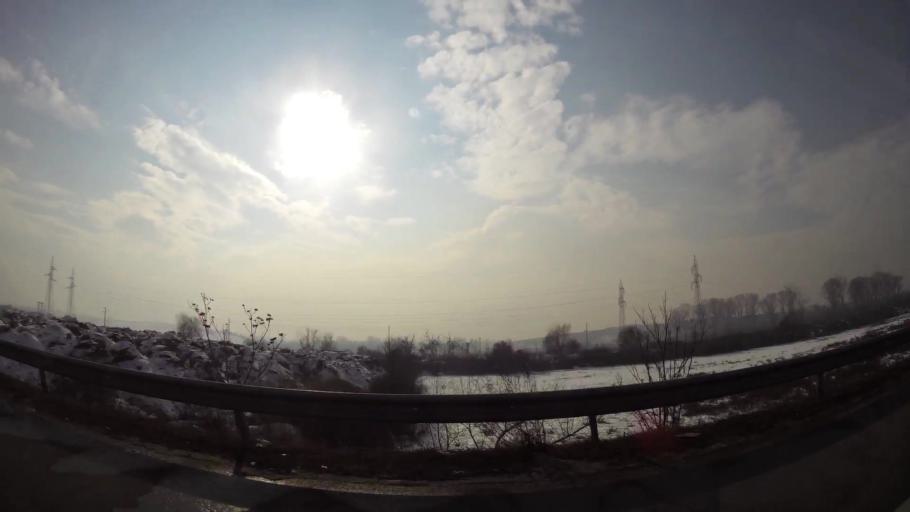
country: MK
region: Butel
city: Butel
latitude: 42.0353
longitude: 21.4698
